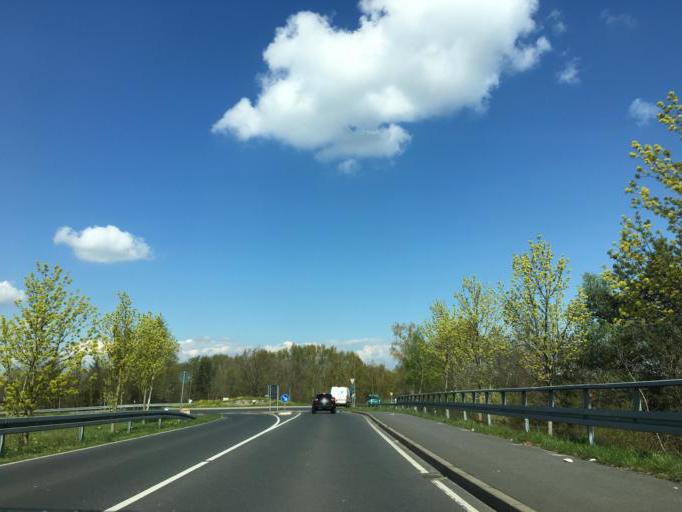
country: DE
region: Hesse
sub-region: Regierungsbezirk Darmstadt
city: Eppertshausen
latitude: 49.9918
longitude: 8.8548
